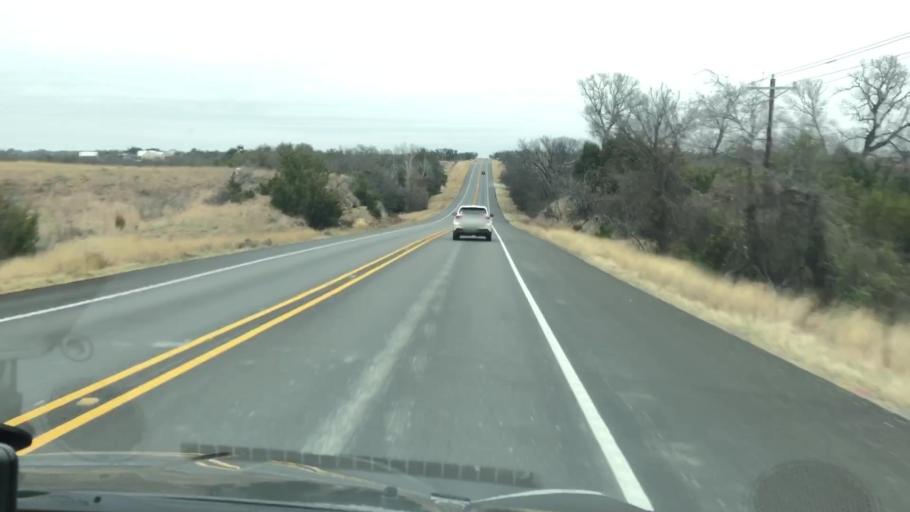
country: US
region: Texas
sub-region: Erath County
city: Stephenville
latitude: 32.3134
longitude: -98.1837
